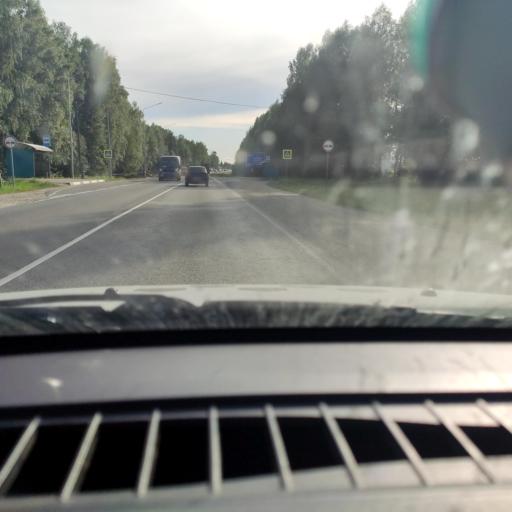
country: RU
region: Kirov
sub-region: Kirovo-Chepetskiy Rayon
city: Kirov
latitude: 58.6361
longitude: 49.8349
